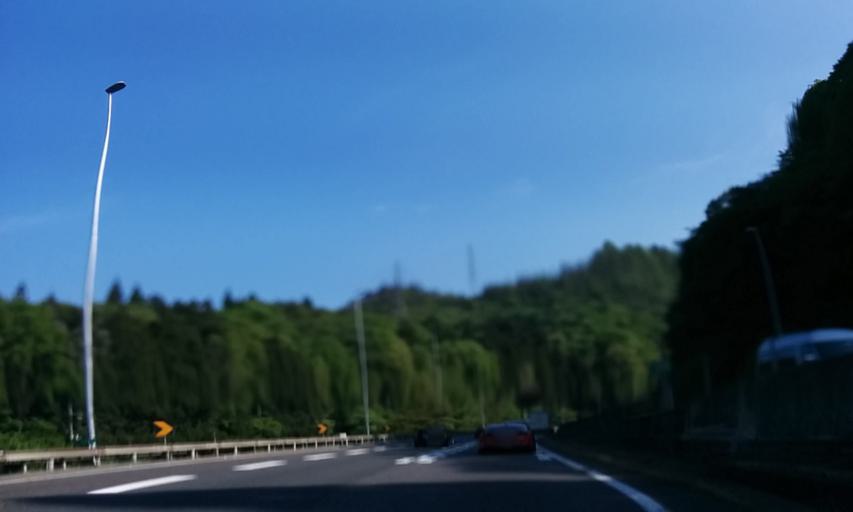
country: JP
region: Shiga Prefecture
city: Hikone
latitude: 35.2937
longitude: 136.2978
